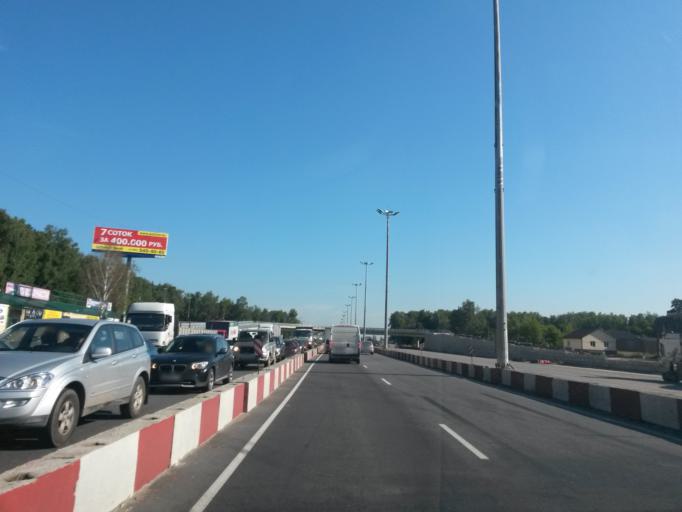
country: RU
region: Moskovskaya
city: Bolshevo
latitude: 55.9388
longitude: 37.8120
